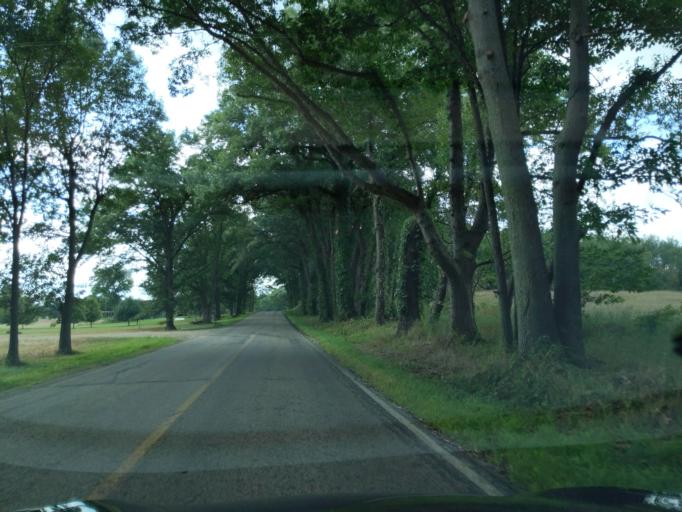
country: US
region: Michigan
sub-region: Eaton County
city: Eaton Rapids
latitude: 42.3786
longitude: -84.6104
